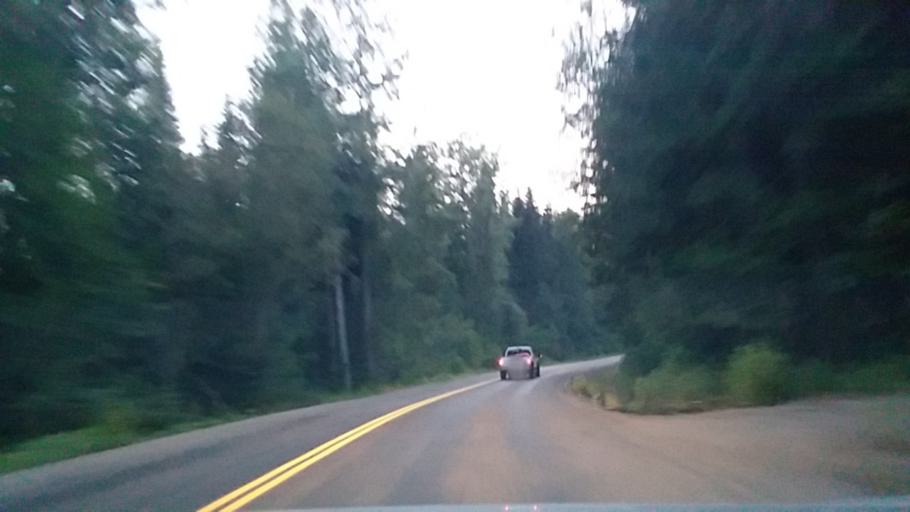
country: US
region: Washington
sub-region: Kittitas County
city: Cle Elum
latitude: 47.3144
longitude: -121.2869
